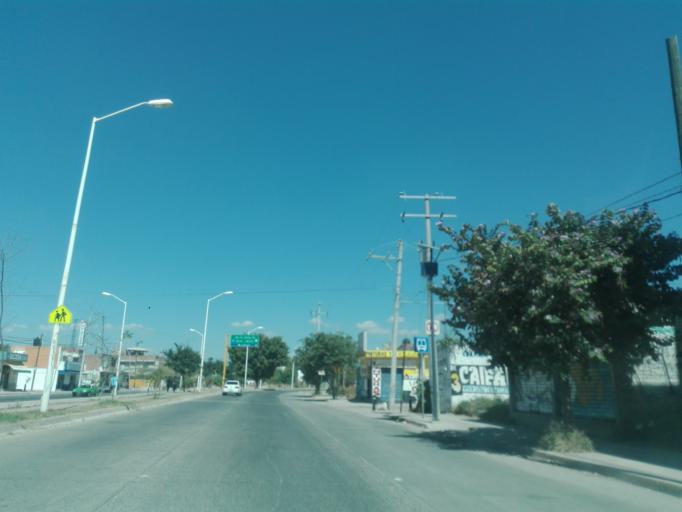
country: MX
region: Guanajuato
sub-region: Leon
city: San Jose de Duran (Los Troncoso)
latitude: 21.0739
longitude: -101.6363
